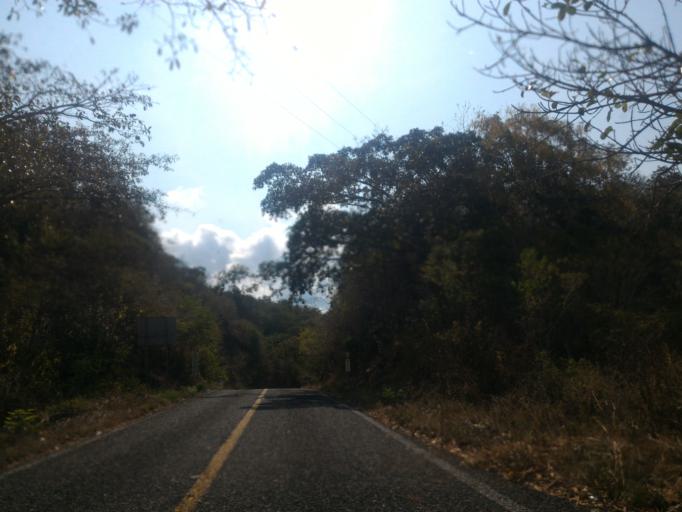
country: MX
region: Michoacan
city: Coahuayana Viejo
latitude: 18.4730
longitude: -103.5584
